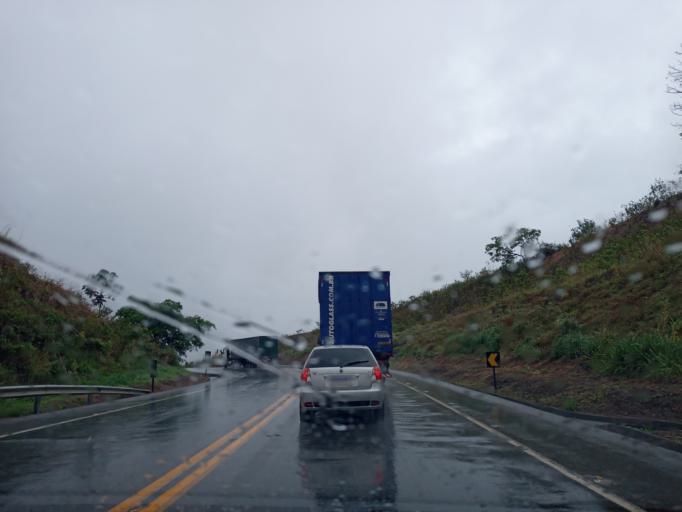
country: BR
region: Minas Gerais
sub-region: Luz
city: Luz
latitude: -19.7176
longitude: -45.8817
